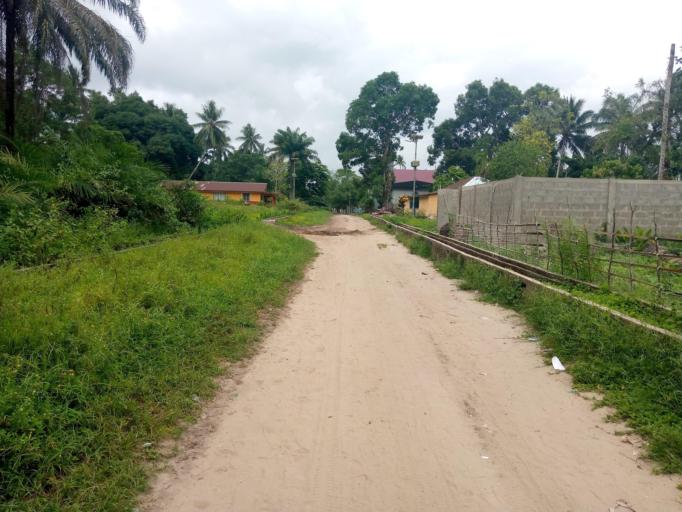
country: SL
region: Southern Province
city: Bonthe
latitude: 7.5264
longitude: -12.5029
